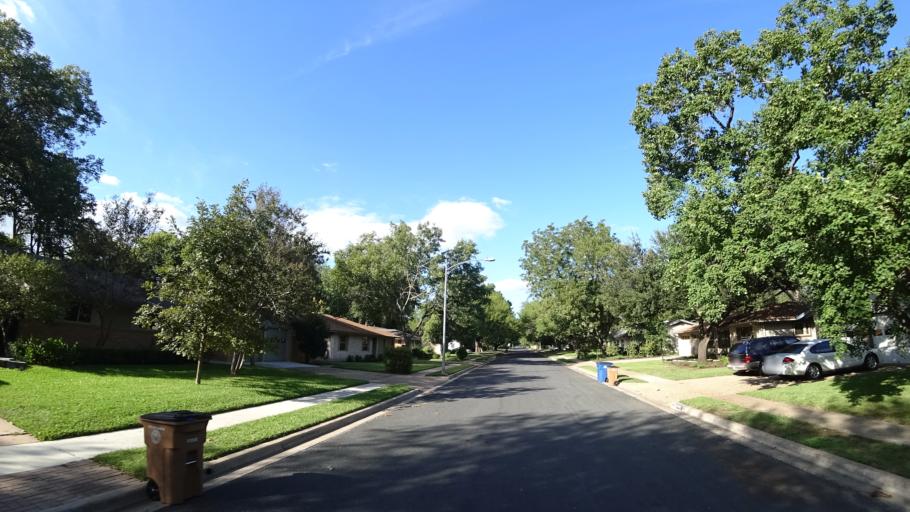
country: US
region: Texas
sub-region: Williamson County
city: Jollyville
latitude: 30.3696
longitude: -97.7367
